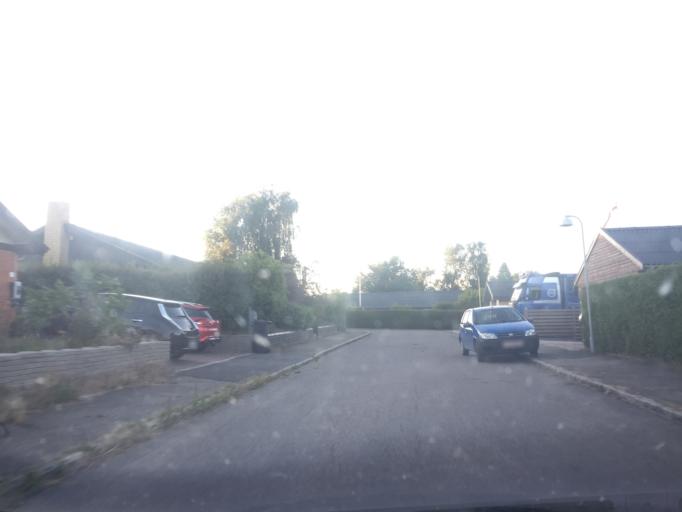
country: DK
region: Capital Region
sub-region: Gribskov Kommune
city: Helsinge
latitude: 56.0134
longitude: 12.2038
